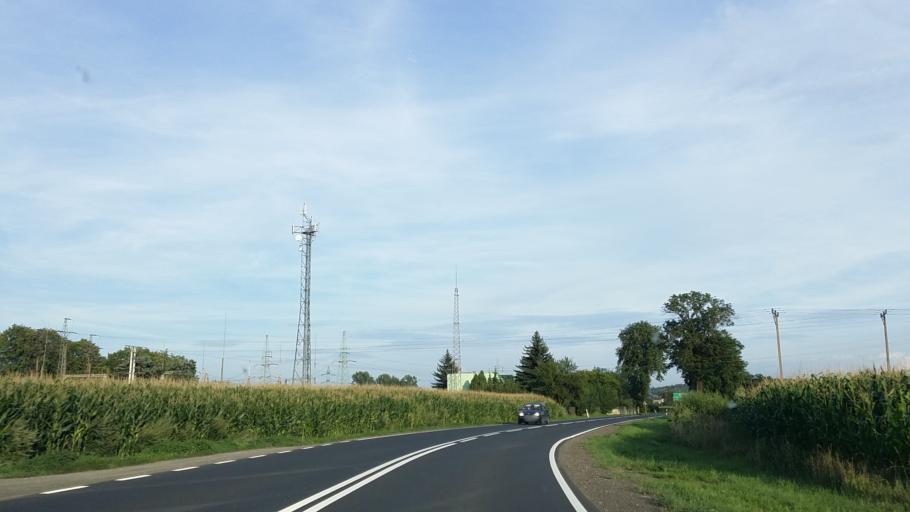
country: PL
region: Lesser Poland Voivodeship
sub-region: Powiat oswiecimski
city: Zator
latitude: 49.9991
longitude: 19.4519
